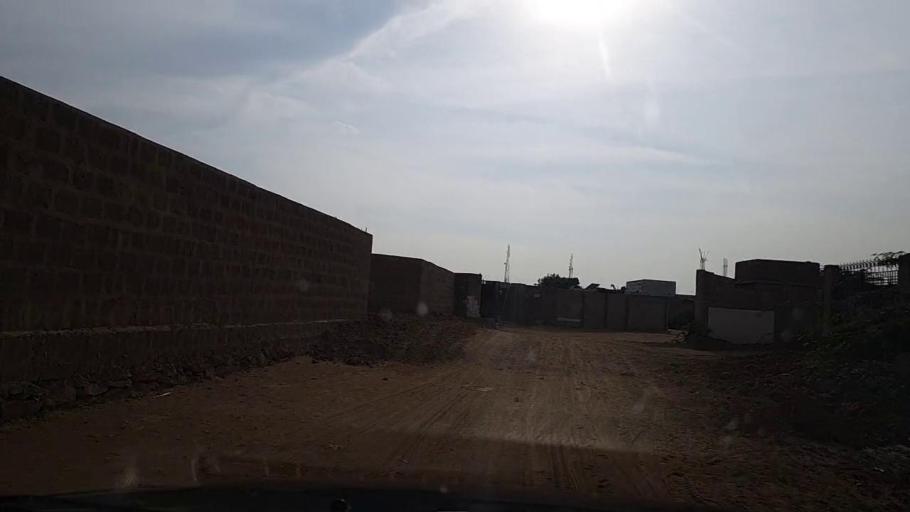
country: PK
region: Sindh
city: Gharo
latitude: 24.7939
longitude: 67.5323
